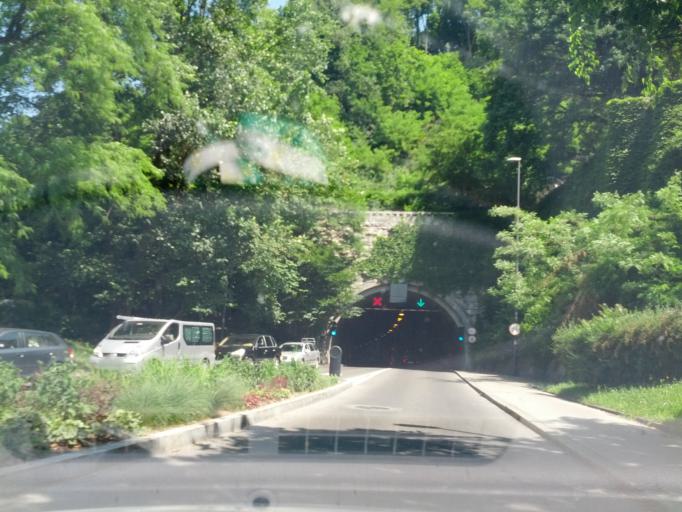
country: SI
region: Ljubljana
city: Ljubljana
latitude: 46.0449
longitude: 14.5097
